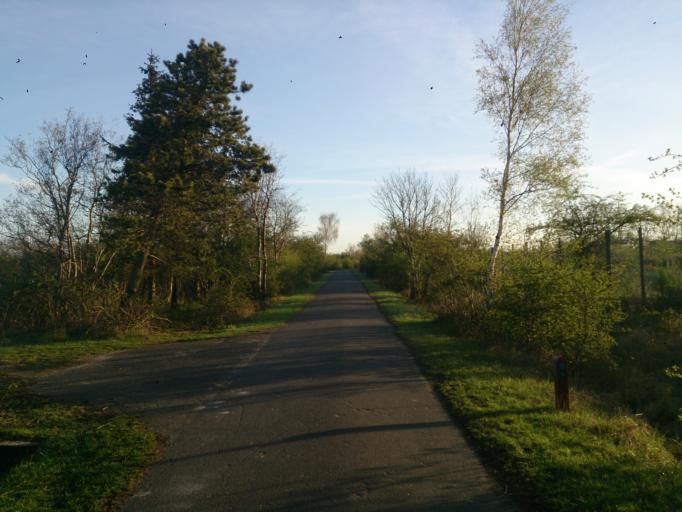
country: DK
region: Capital Region
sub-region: Tarnby Kommune
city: Tarnby
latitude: 55.6021
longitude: 12.5745
